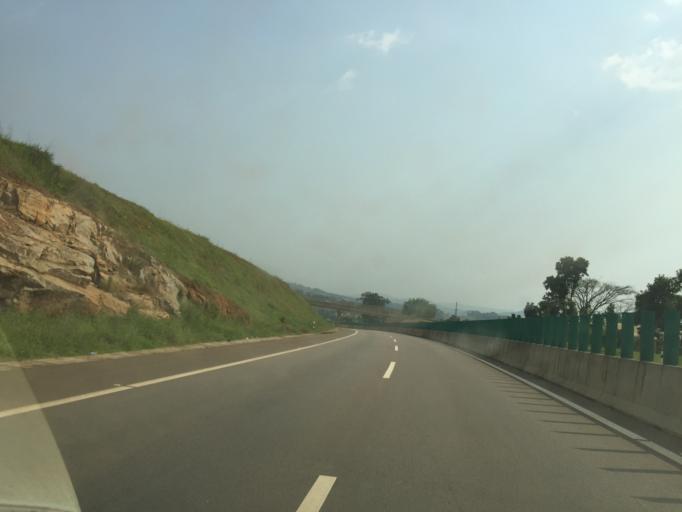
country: UG
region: Central Region
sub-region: Wakiso District
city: Kajansi
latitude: 0.2618
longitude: 32.5207
